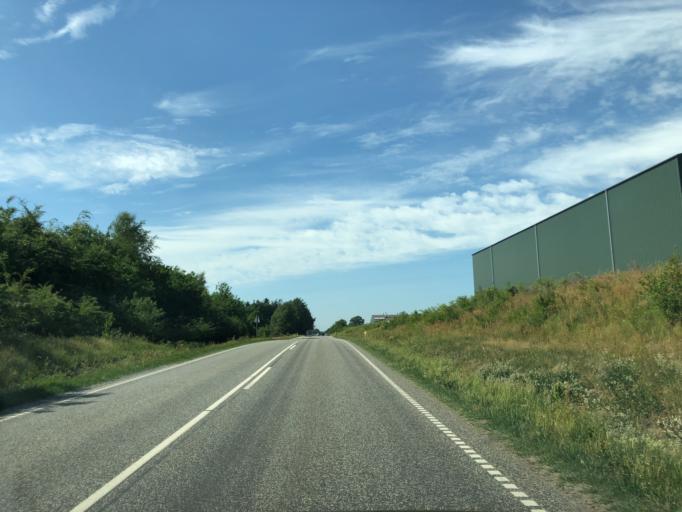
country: DK
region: Central Jutland
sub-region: Ikast-Brande Kommune
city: Brande
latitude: 55.9037
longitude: 9.1970
